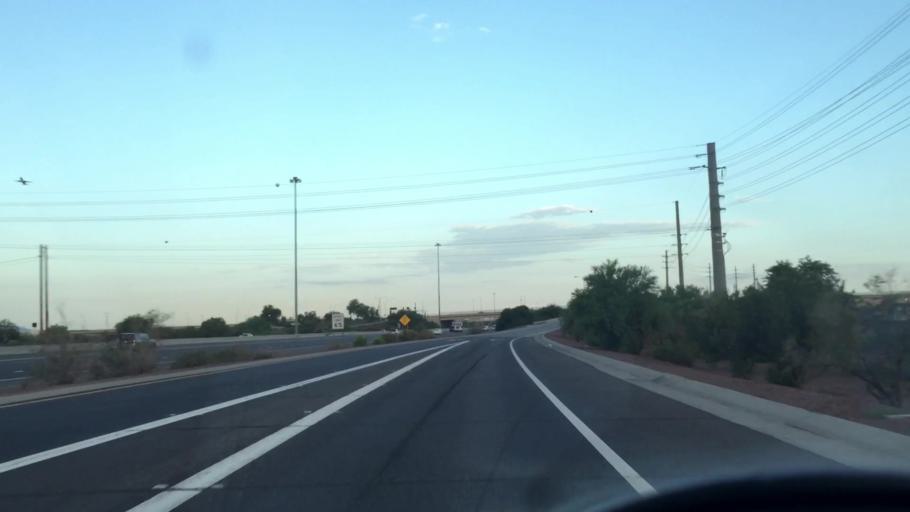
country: US
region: Arizona
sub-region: Maricopa County
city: Tempe Junction
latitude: 33.4369
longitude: -111.9549
